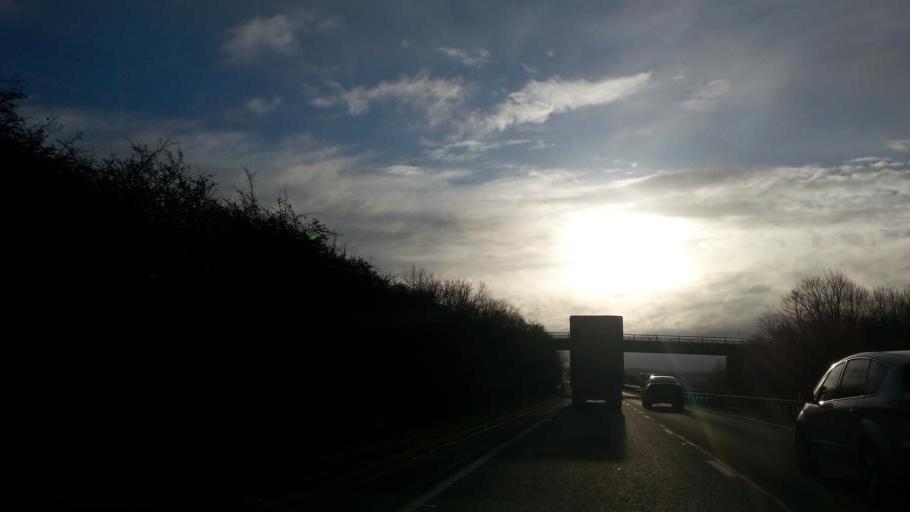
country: GB
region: England
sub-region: Cambridgeshire
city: Great Stukeley
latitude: 52.3574
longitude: -0.2322
